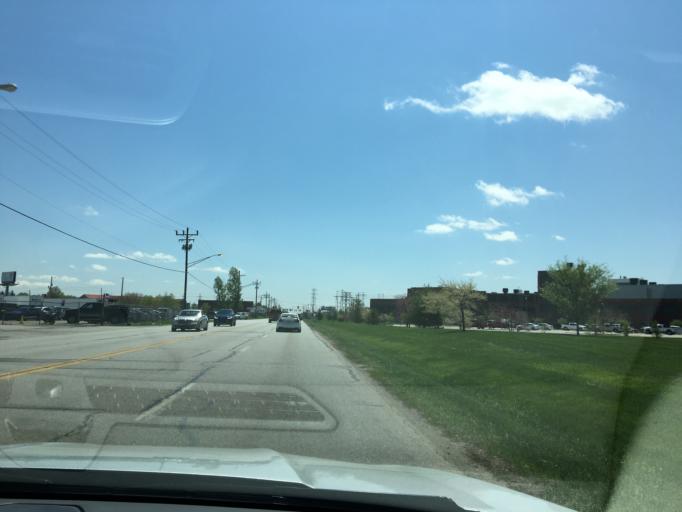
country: US
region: Indiana
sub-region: Tippecanoe County
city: Lafayette
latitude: 40.4035
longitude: -86.8616
